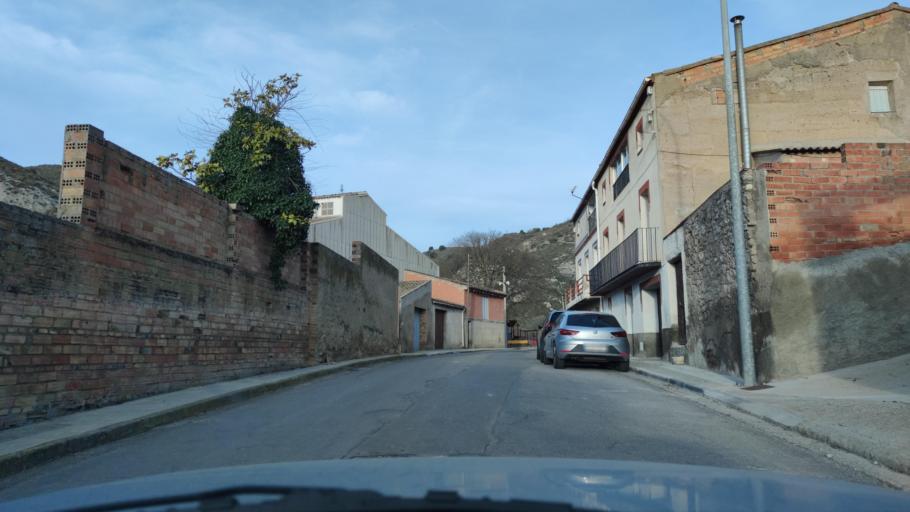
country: ES
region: Catalonia
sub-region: Provincia de Lleida
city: Balaguer
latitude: 41.8230
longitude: 0.8037
